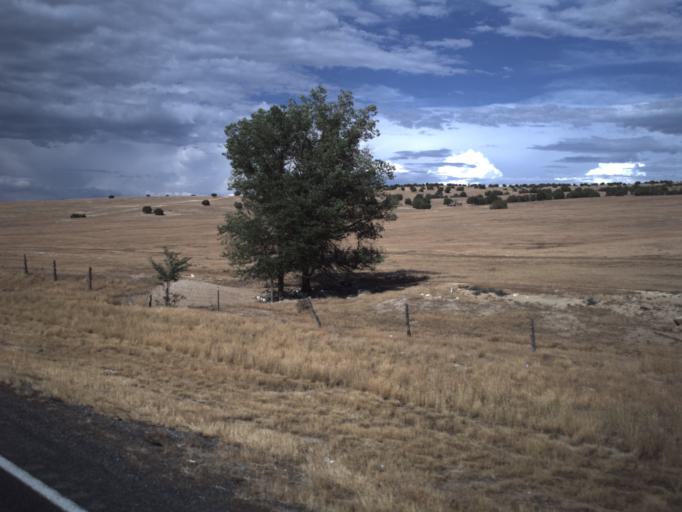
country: US
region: Utah
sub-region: Sanpete County
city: Ephraim
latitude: 39.4110
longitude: -111.5613
